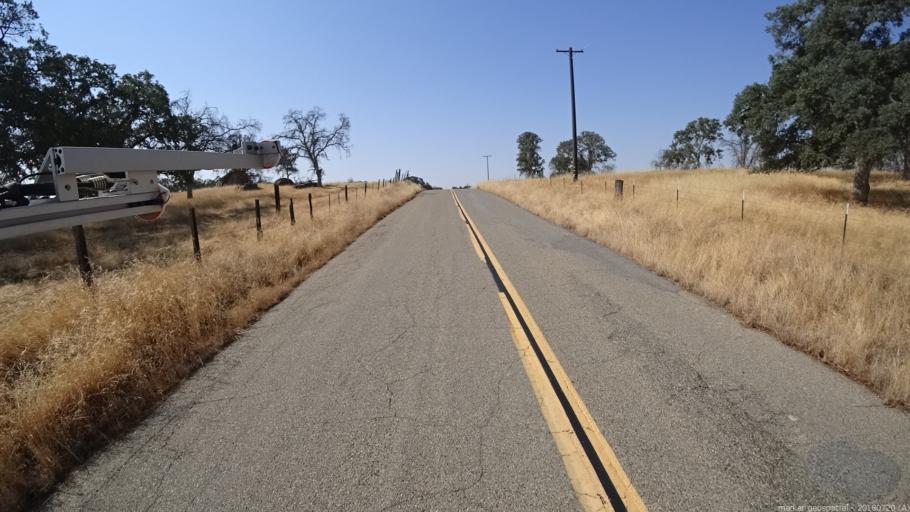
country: US
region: California
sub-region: Madera County
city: Yosemite Lakes
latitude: 37.2446
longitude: -119.9250
